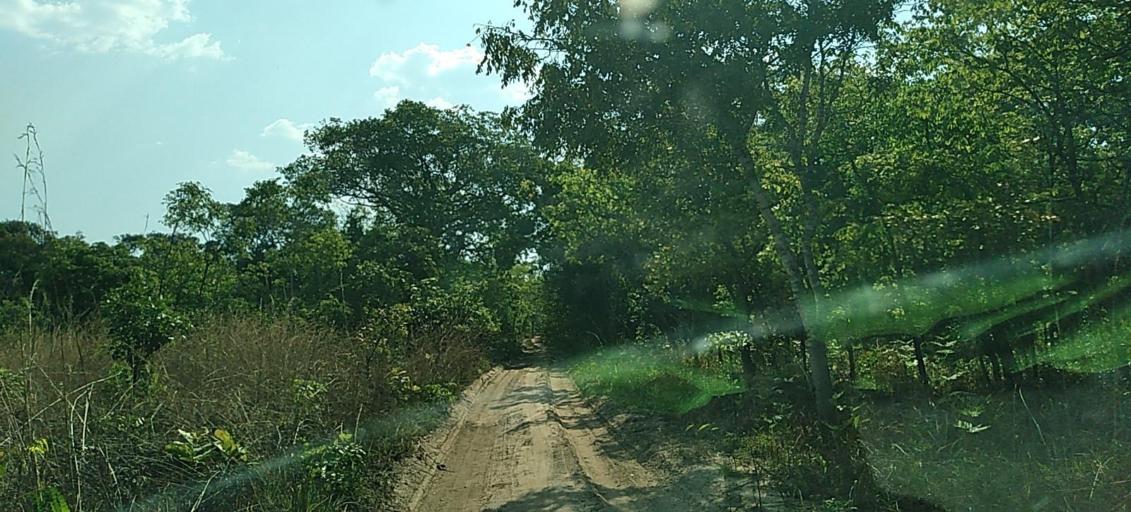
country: ZM
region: North-Western
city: Mwinilunga
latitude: -11.3027
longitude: 24.8379
